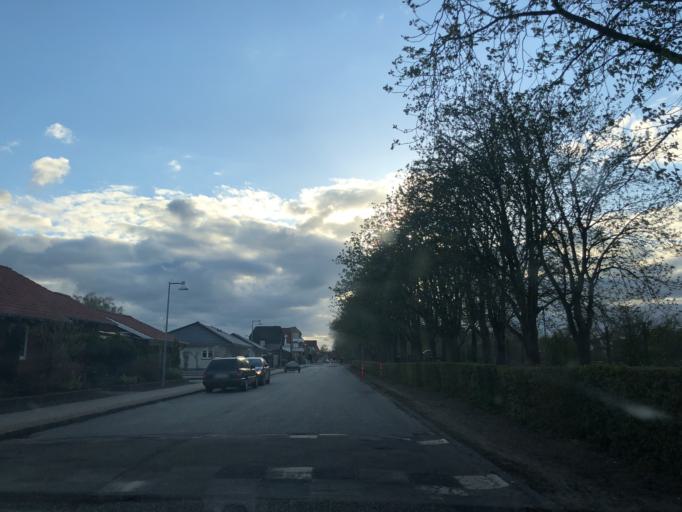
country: DK
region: Zealand
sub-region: Ringsted Kommune
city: Ringsted
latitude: 55.4454
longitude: 11.8042
